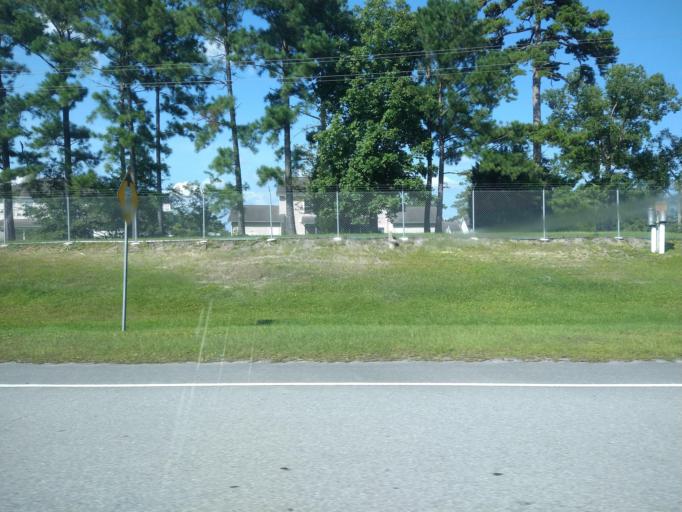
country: US
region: North Carolina
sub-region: Onslow County
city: Piney Green
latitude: 34.7316
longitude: -77.3492
